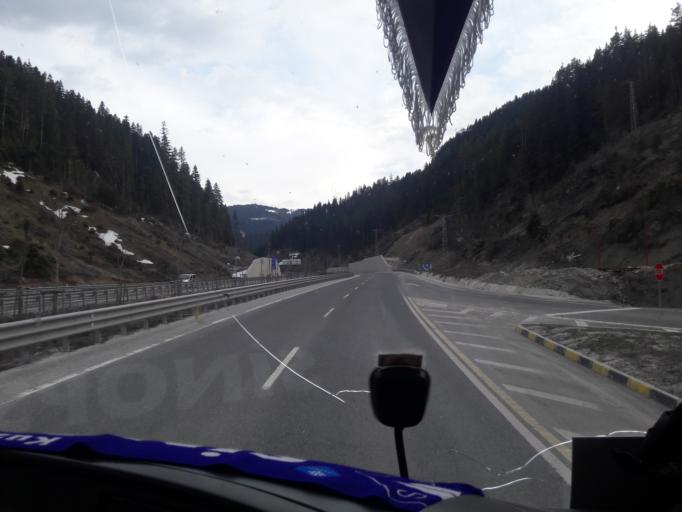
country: TR
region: Kastamonu
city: Kuzyaka
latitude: 41.0992
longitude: 33.7509
